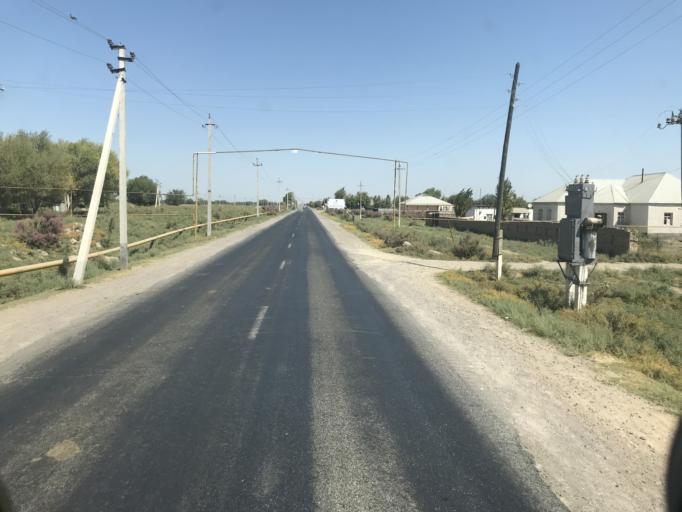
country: KZ
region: Ongtustik Qazaqstan
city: Ilyich
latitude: 40.8942
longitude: 68.4882
